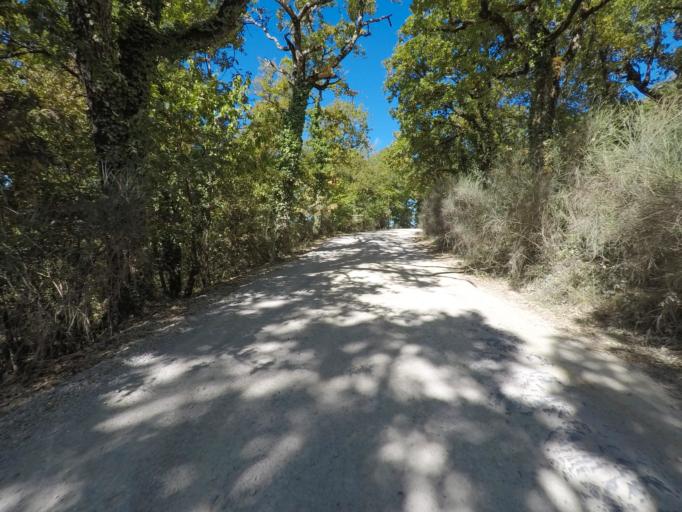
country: IT
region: Tuscany
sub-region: Provincia di Siena
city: Castellina in Chianti
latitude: 43.4295
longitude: 11.3336
